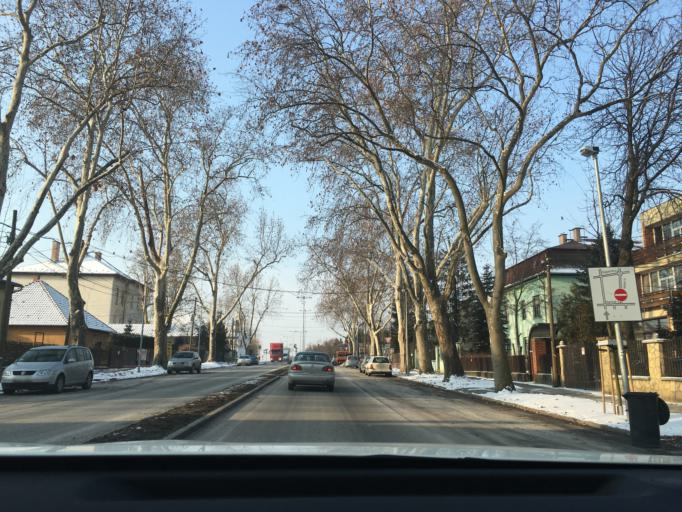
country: HU
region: Budapest
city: Budapest X. keruelet
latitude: 47.4842
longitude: 19.1468
